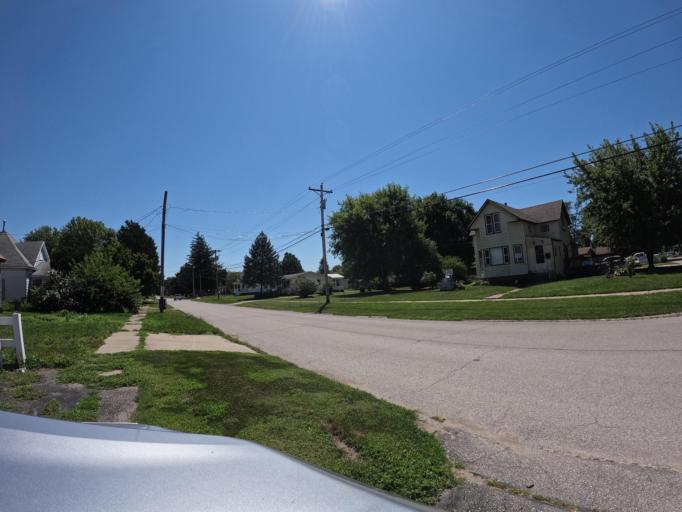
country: US
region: Iowa
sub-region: Monroe County
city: Albia
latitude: 41.0272
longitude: -92.7943
